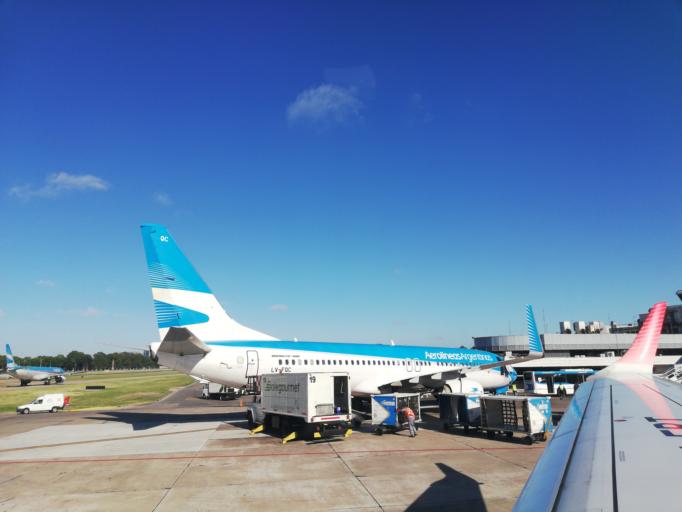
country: AR
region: Buenos Aires F.D.
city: Colegiales
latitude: -34.5574
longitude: -58.4157
